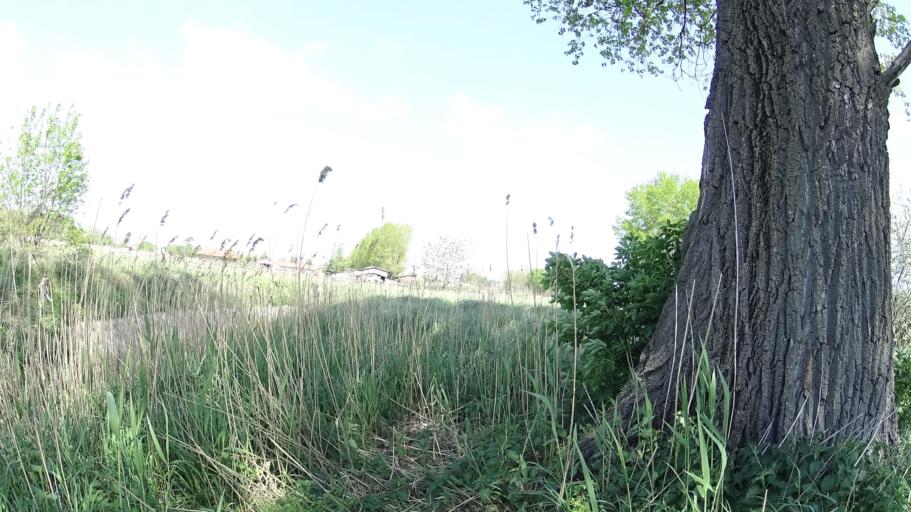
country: HU
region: Pest
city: Vecses
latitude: 47.3960
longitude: 19.2937
